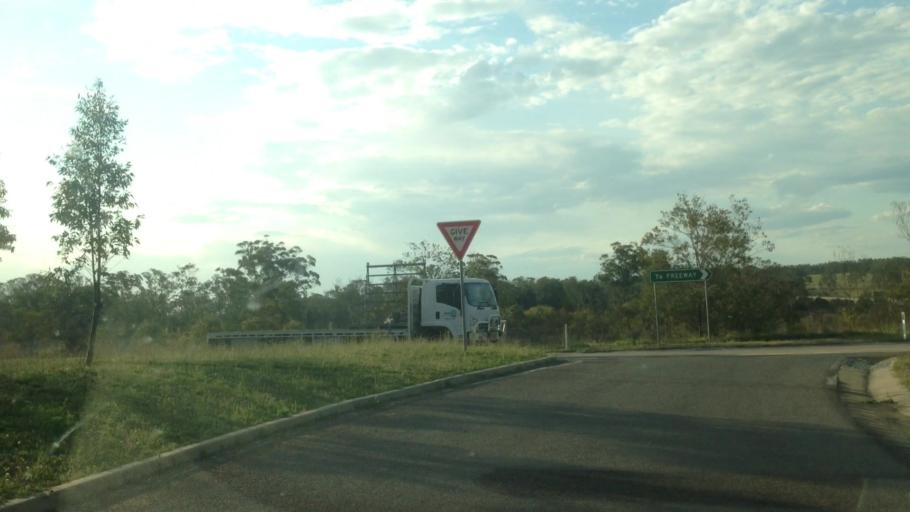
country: AU
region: New South Wales
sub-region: Cessnock
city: Heddon Greta
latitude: -32.8438
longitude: 151.5422
